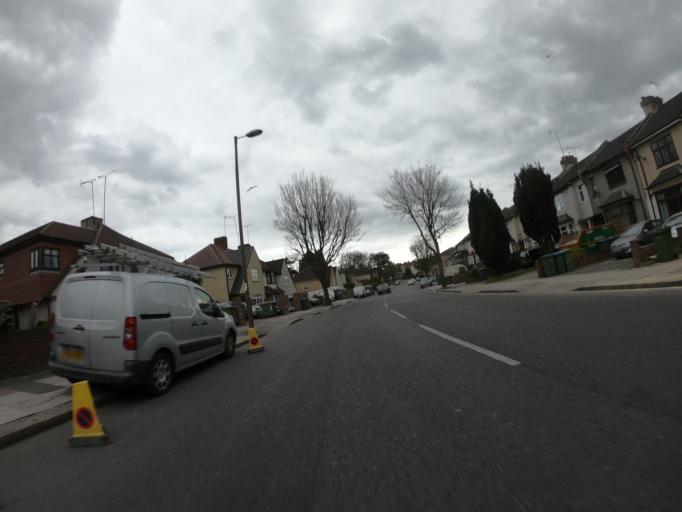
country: GB
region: England
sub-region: Greater London
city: Abbey Wood
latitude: 51.4769
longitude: 0.1080
